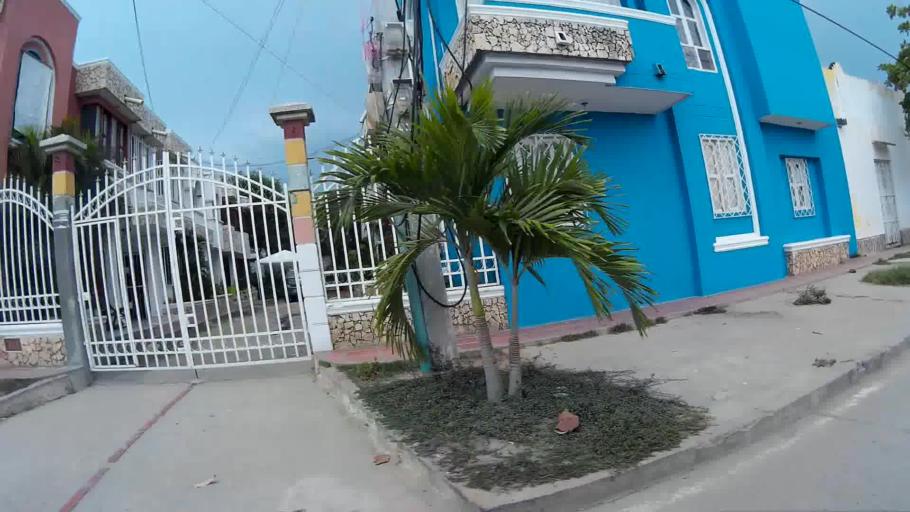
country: CO
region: Magdalena
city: Cienaga
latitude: 11.0122
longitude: -74.2452
